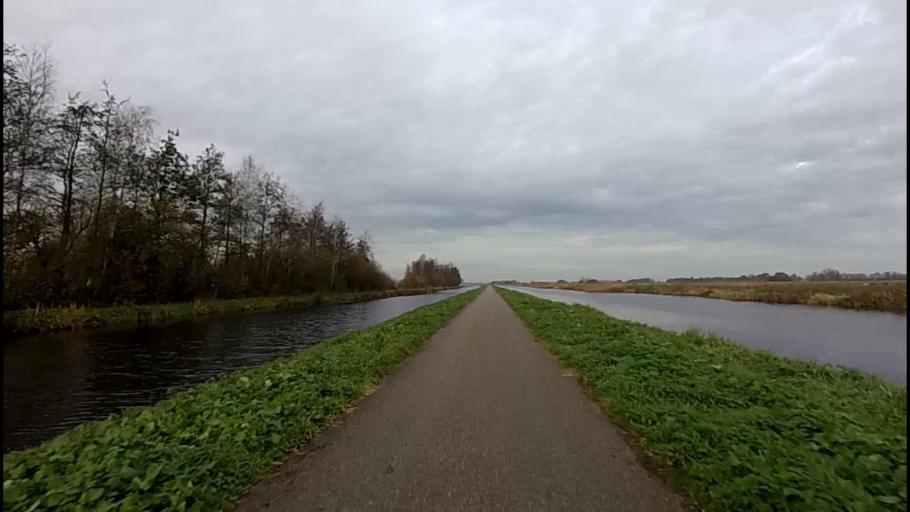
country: NL
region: South Holland
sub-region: Molenwaard
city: Nieuw-Lekkerland
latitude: 51.9370
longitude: 4.7377
